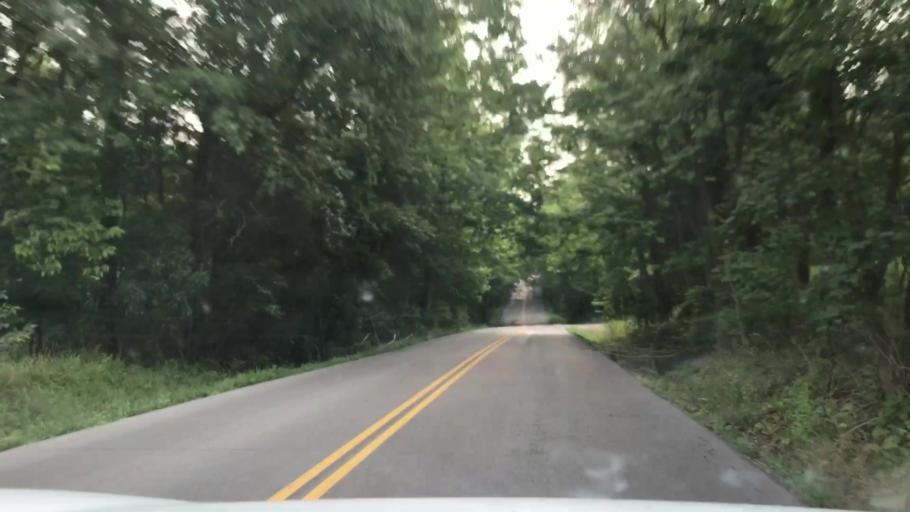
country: US
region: Missouri
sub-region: Saint Charles County
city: Weldon Spring
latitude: 38.7050
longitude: -90.6495
